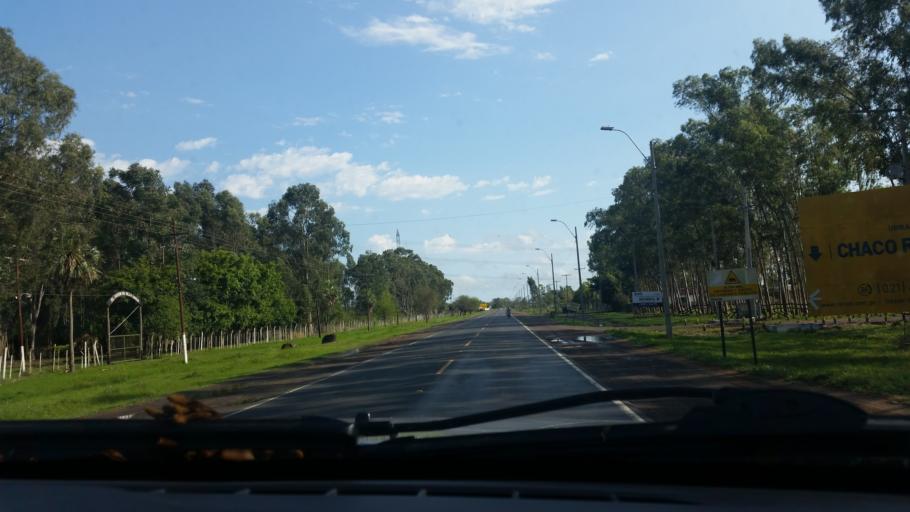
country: PY
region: Presidente Hayes
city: Villa Hayes
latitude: -25.0728
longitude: -57.5319
